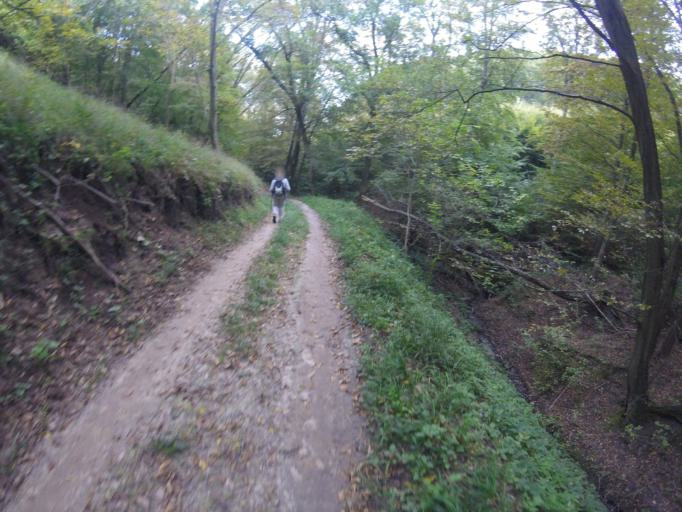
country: HU
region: Pest
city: Szob
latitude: 47.8040
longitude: 18.8296
